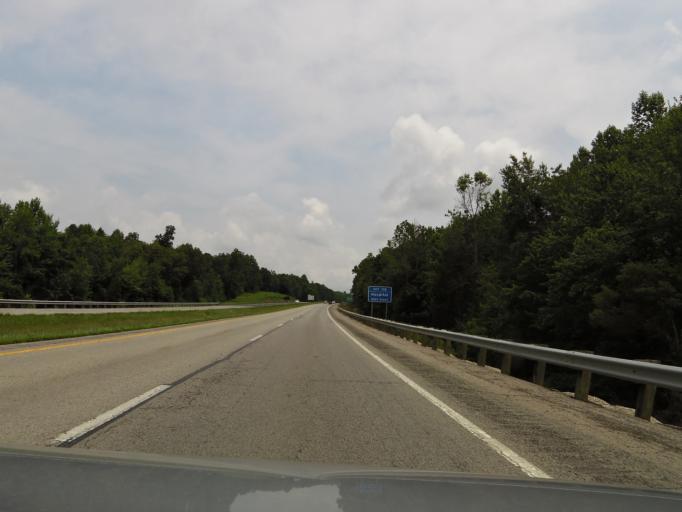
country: US
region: Kentucky
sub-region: Hardin County
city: Elizabethtown
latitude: 37.6675
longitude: -85.8785
